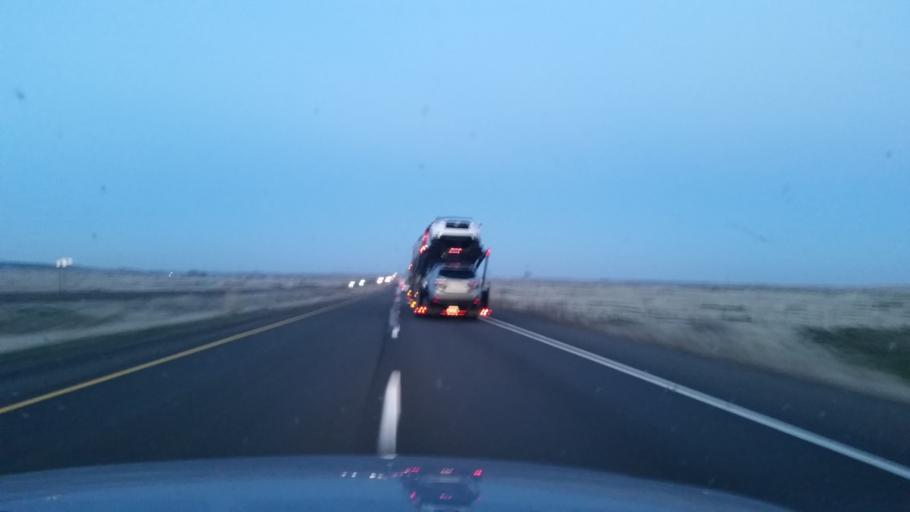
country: US
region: Washington
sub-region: Adams County
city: Ritzville
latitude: 47.1367
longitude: -118.3366
